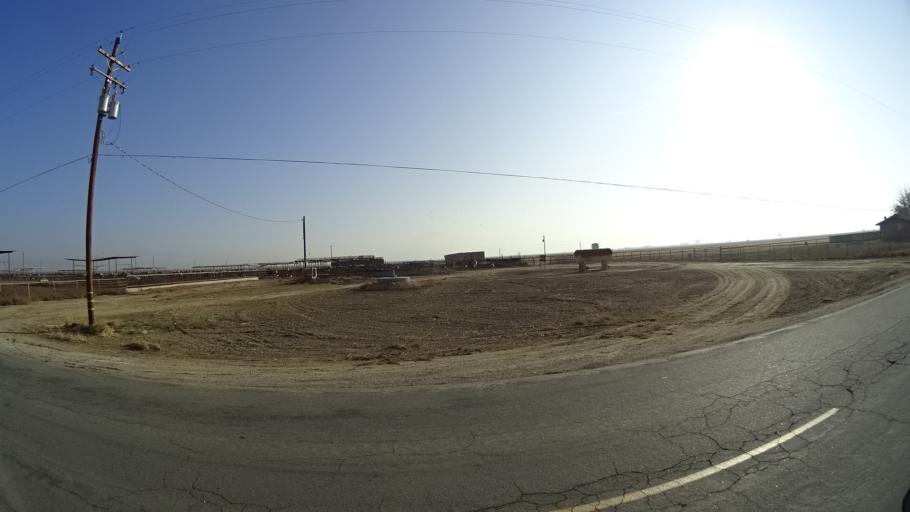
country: US
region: California
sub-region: Kern County
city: Weedpatch
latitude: 35.2203
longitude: -118.9676
